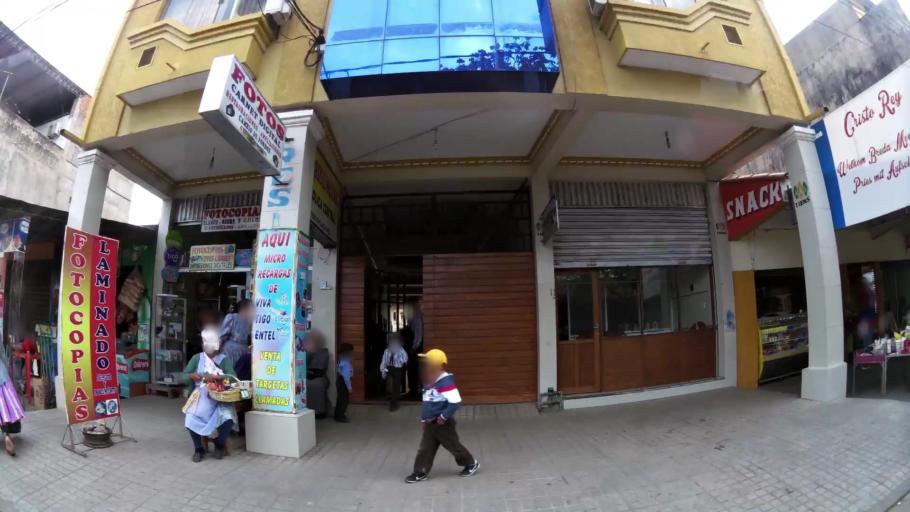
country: BO
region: Santa Cruz
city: Santa Cruz de la Sierra
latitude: -17.7762
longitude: -63.1767
